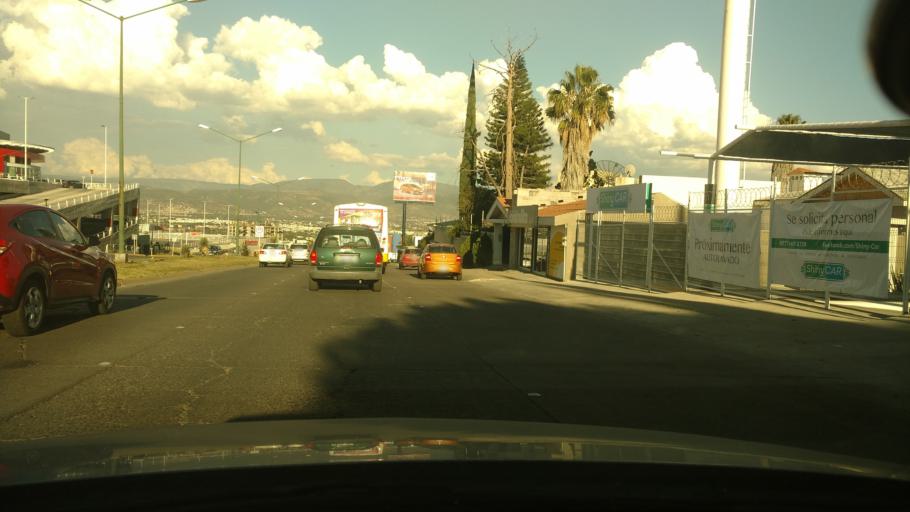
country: MX
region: Guanajuato
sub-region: Leon
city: La Ermita
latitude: 21.1550
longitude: -101.7094
